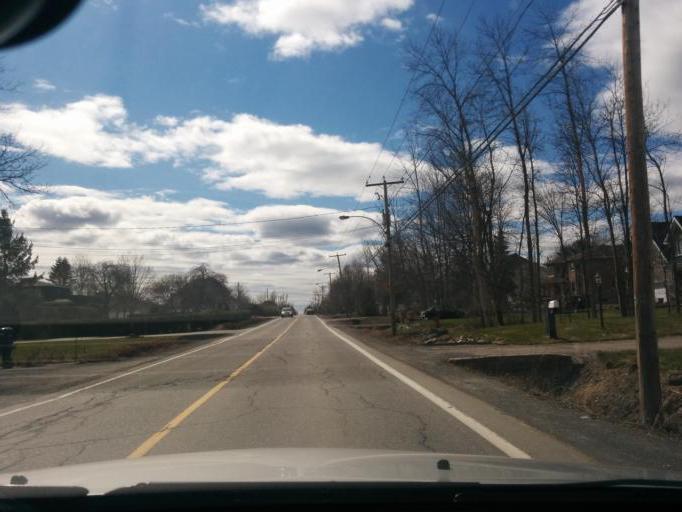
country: CA
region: Ontario
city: Ottawa
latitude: 45.4136
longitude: -75.7929
